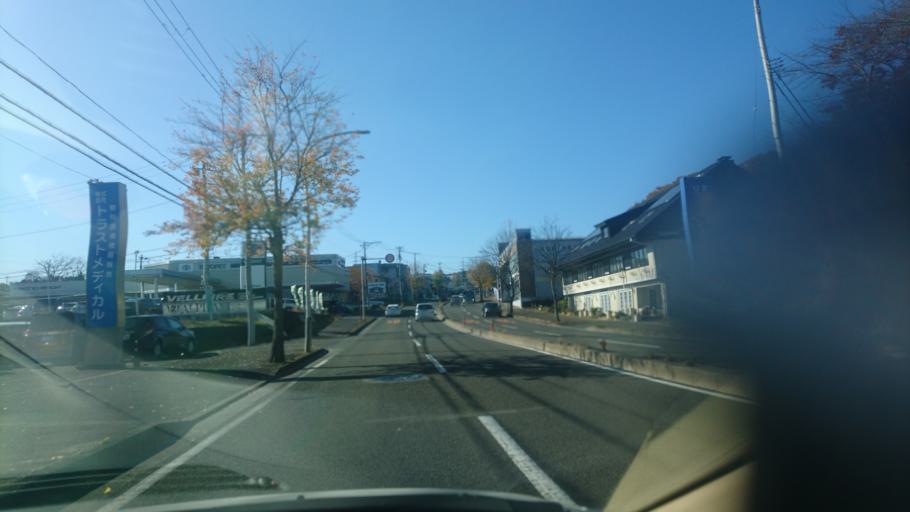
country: JP
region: Miyagi
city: Sendai-shi
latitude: 38.3090
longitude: 140.8425
